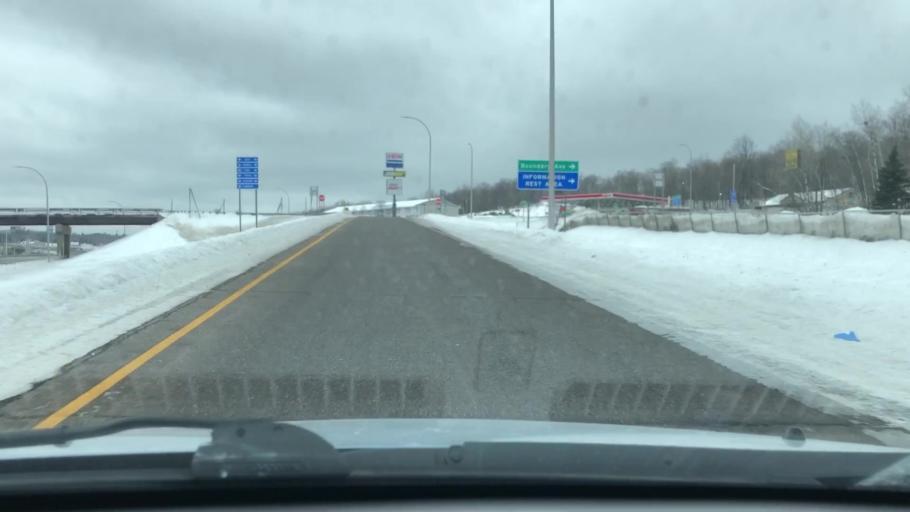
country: US
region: Minnesota
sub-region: Saint Louis County
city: Proctor
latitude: 46.7264
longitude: -92.2155
